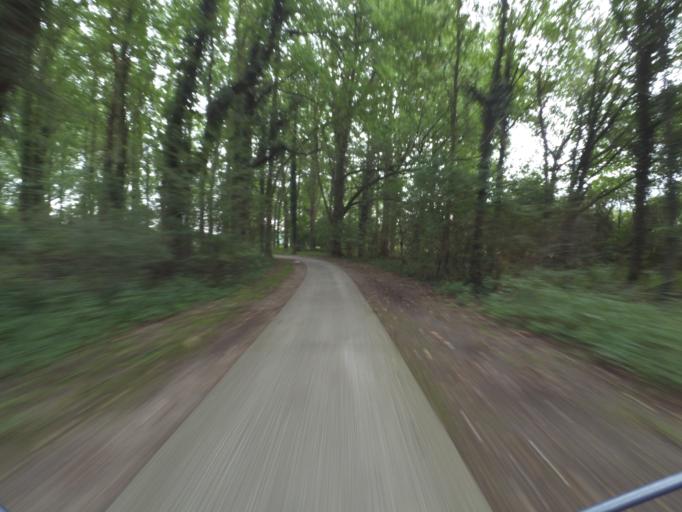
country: NL
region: Overijssel
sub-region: Gemeente Losser
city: Losser
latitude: 52.2836
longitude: 7.0243
